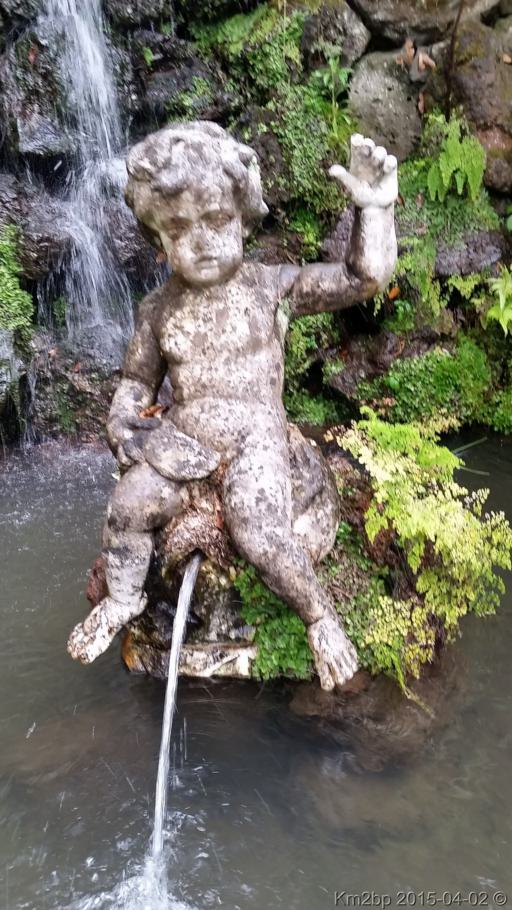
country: PT
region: Madeira
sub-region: Funchal
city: Nossa Senhora do Monte
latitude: 32.6752
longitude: -16.9012
